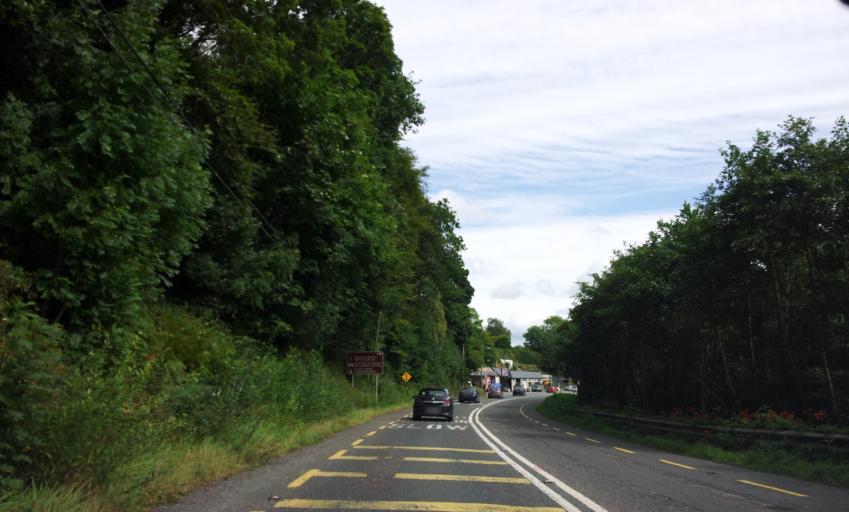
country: IE
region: Munster
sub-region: Ciarrai
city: Cill Airne
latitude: 52.0753
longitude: -9.6344
